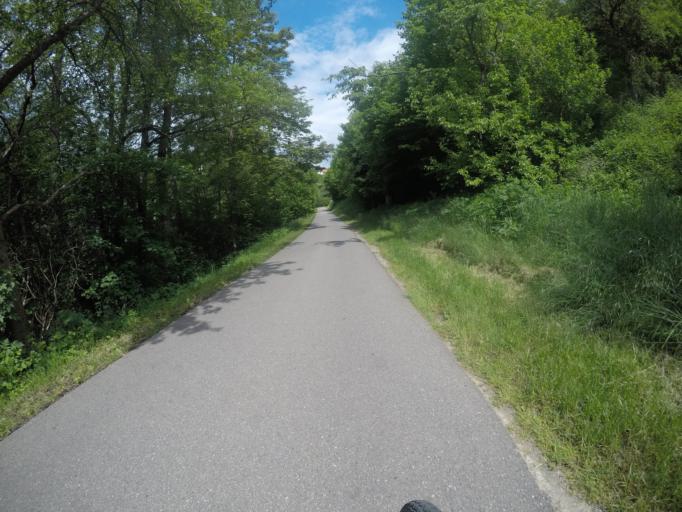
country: DE
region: Baden-Wuerttemberg
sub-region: Karlsruhe Region
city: Wildberg
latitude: 48.6188
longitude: 8.7444
